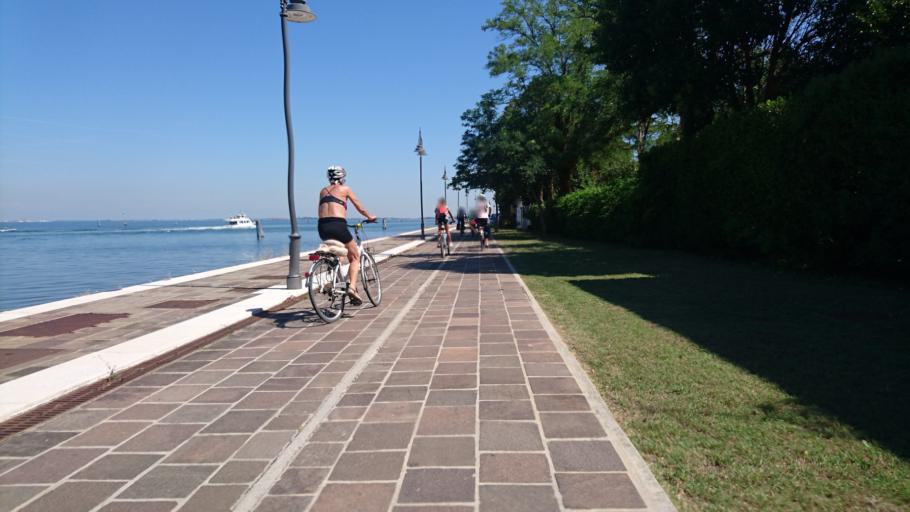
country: IT
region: Veneto
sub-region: Provincia di Venezia
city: San Pietro in Volta
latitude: 45.3437
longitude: 12.3098
